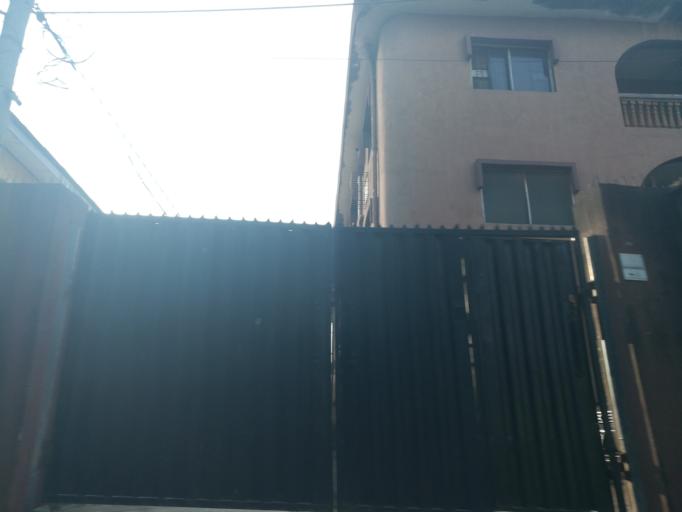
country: NG
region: Lagos
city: Ojota
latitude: 6.5922
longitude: 3.3948
